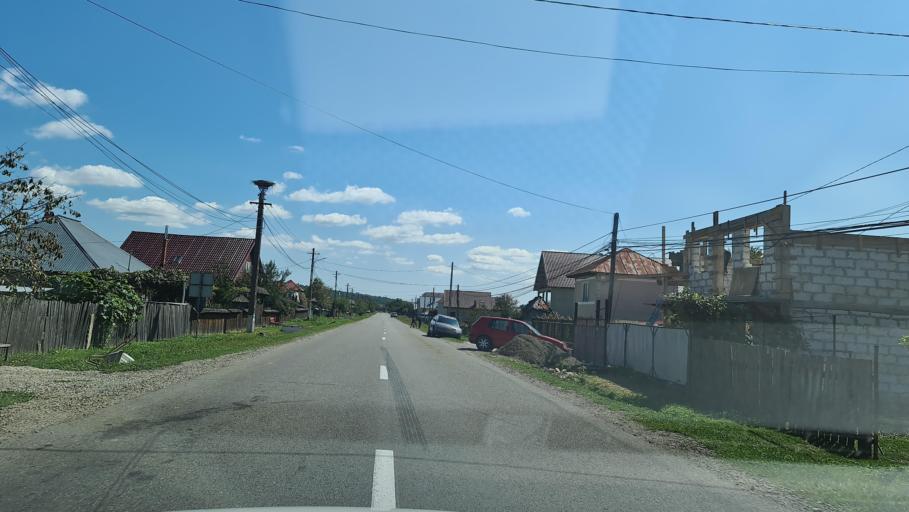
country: RO
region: Bacau
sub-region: Comuna Balcani
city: Frumoasa
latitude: 46.6527
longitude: 26.5564
